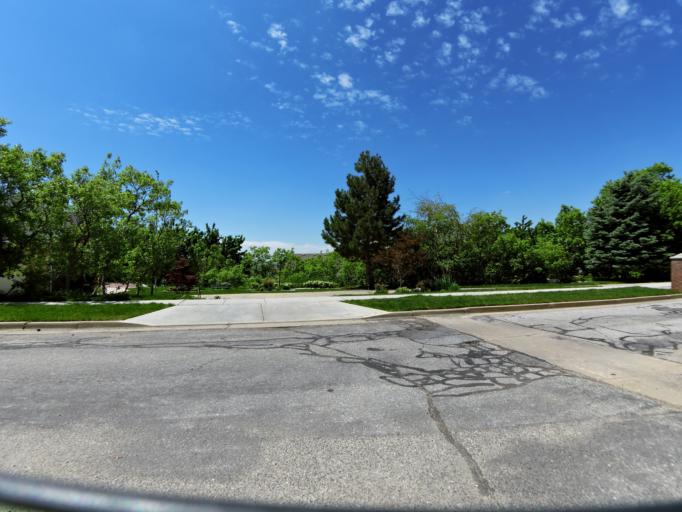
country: US
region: Utah
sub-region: Weber County
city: Uintah
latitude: 41.1625
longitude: -111.9207
